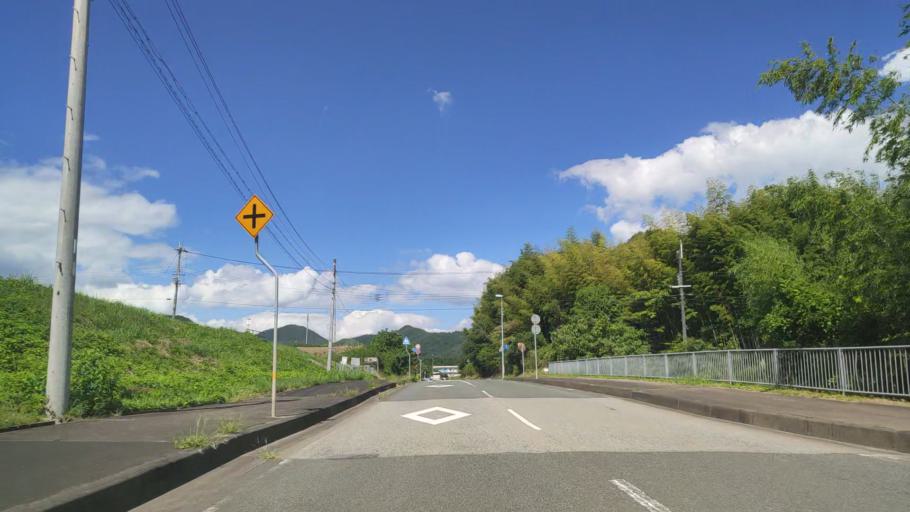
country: JP
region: Kyoto
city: Fukuchiyama
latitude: 35.2313
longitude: 135.1283
